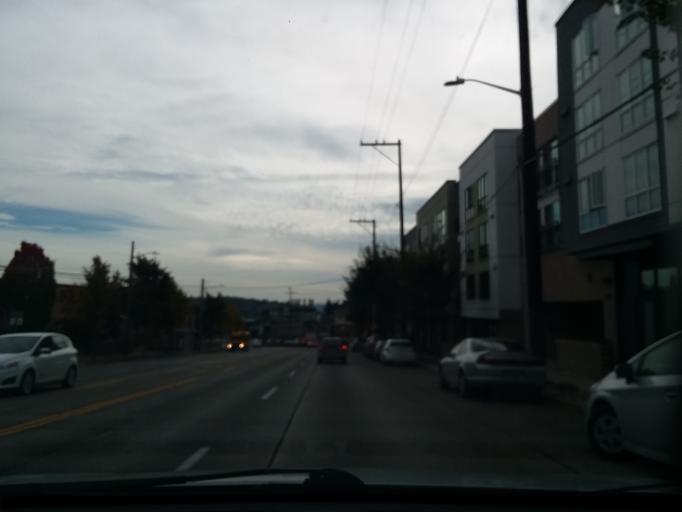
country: US
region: Washington
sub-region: King County
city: Seattle
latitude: 47.6775
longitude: -122.3769
